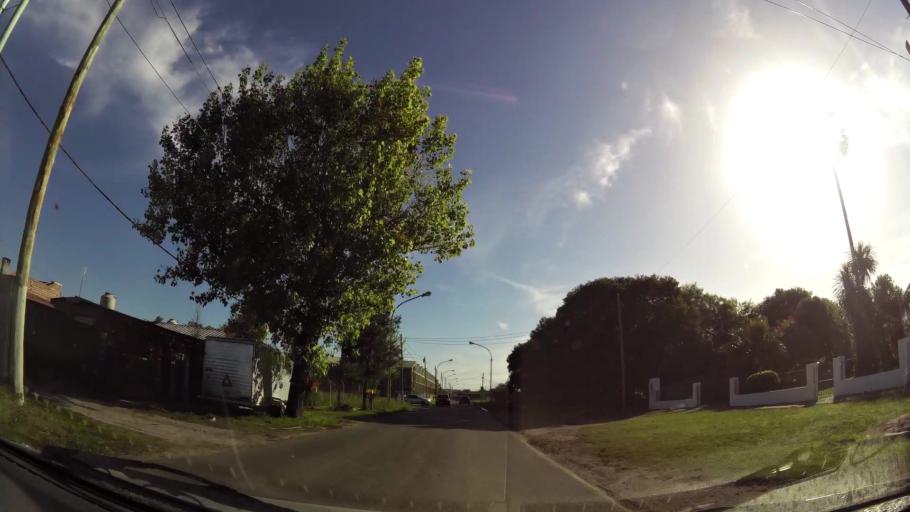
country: AR
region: Buenos Aires
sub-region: Partido de Quilmes
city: Quilmes
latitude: -34.7984
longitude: -58.2164
